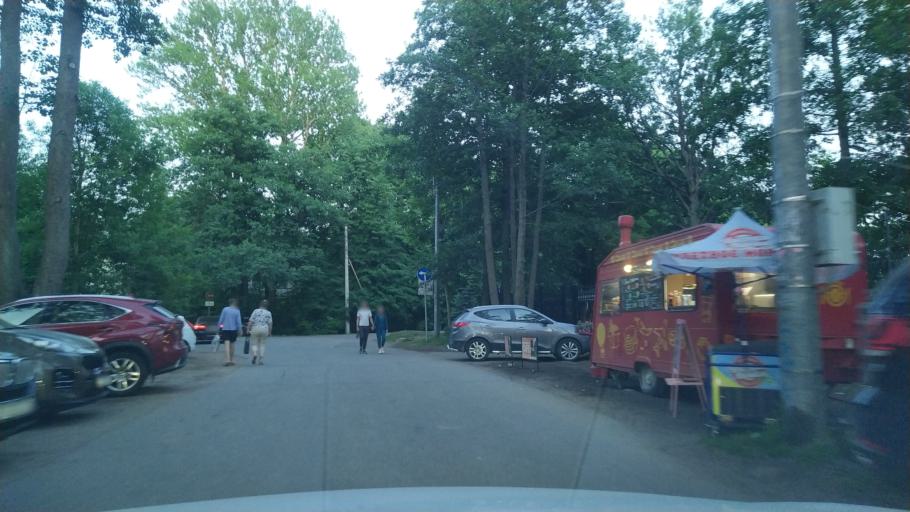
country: RU
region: St.-Petersburg
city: Sestroretsk
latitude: 60.0928
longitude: 29.9416
